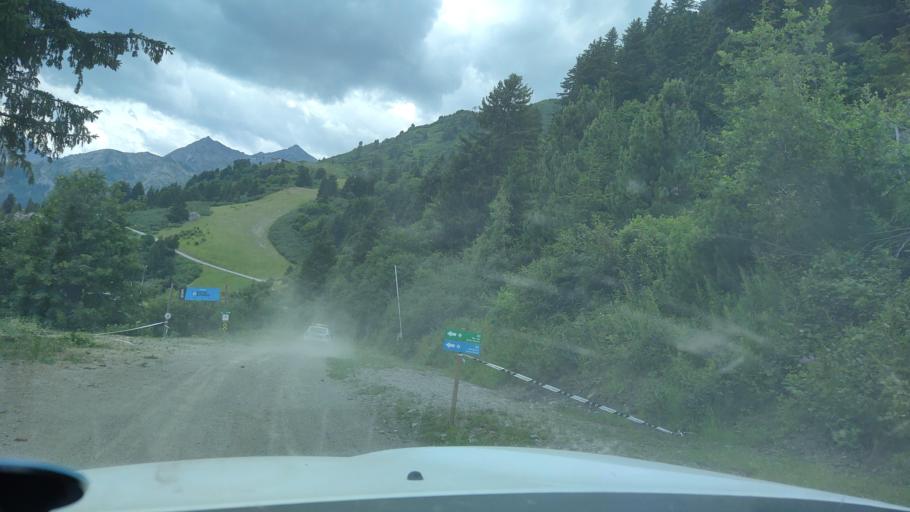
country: FR
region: Rhone-Alpes
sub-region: Departement de la Savoie
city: Meribel
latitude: 45.3753
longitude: 6.5667
